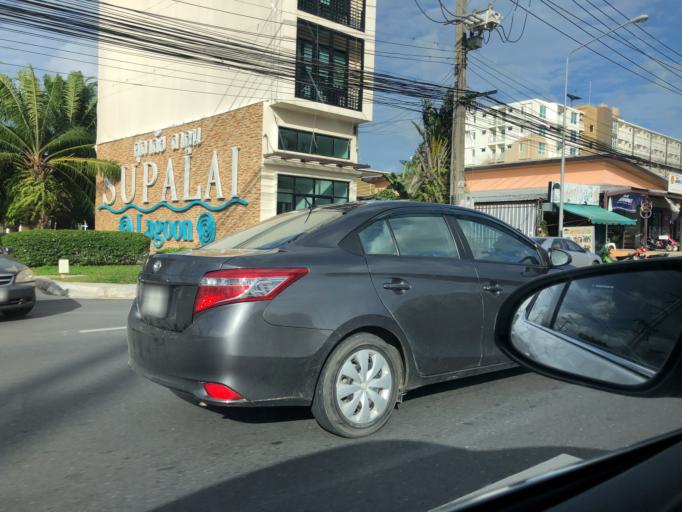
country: TH
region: Phuket
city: Ban Ko Kaeo
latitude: 7.9508
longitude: 98.3905
